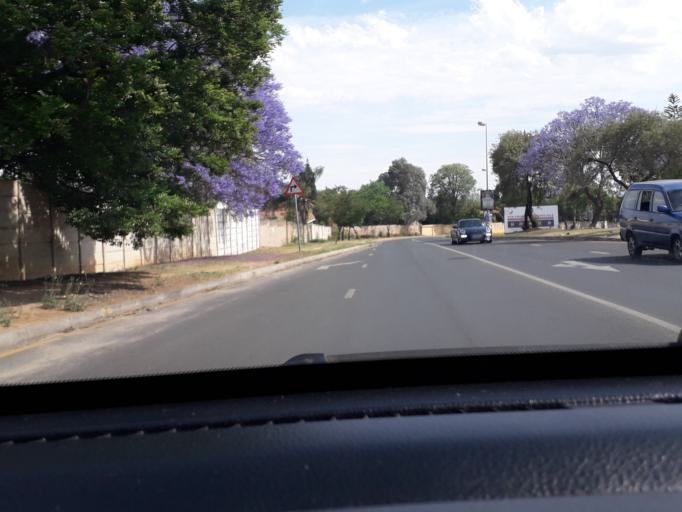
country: ZA
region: Gauteng
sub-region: City of Johannesburg Metropolitan Municipality
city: Midrand
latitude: -25.9829
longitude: 28.1173
